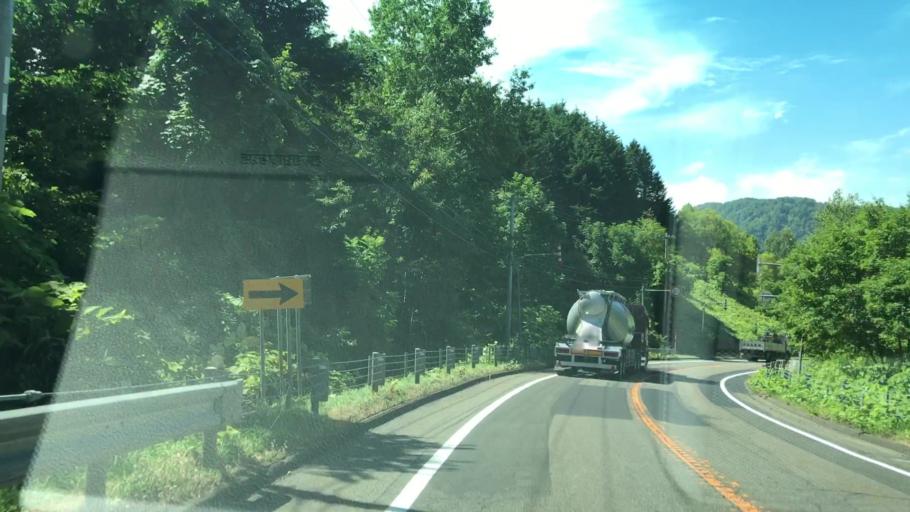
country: JP
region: Hokkaido
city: Shimo-furano
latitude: 42.9010
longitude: 142.4384
